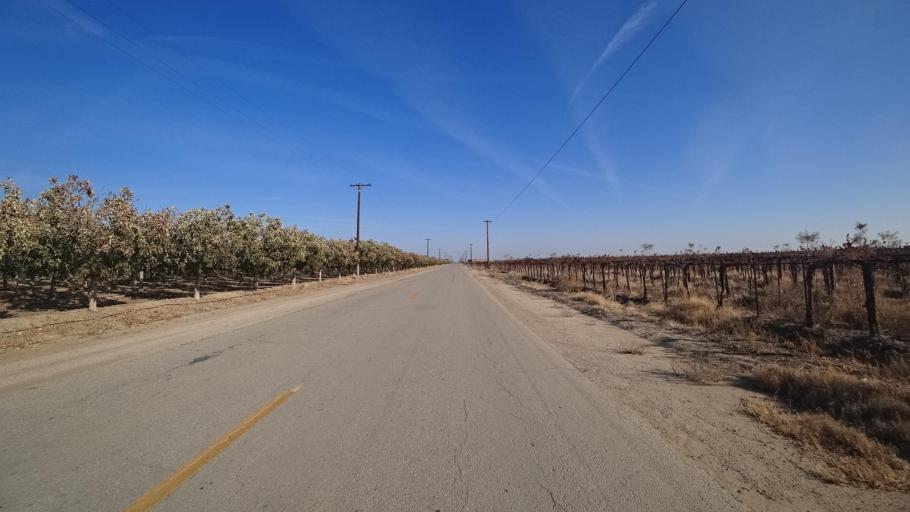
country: US
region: California
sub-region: Kern County
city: Wasco
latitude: 35.7032
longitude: -119.3378
